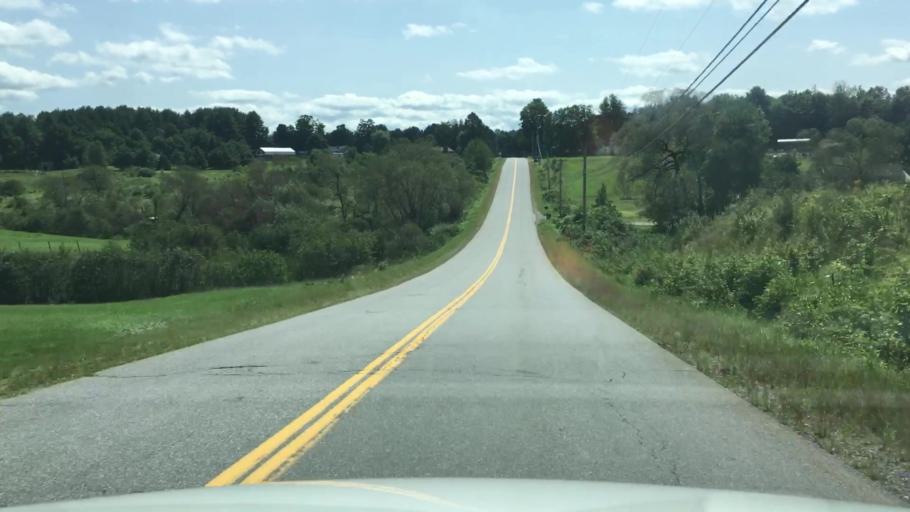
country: US
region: Maine
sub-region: Kennebec County
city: Augusta
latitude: 44.3494
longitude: -69.8122
